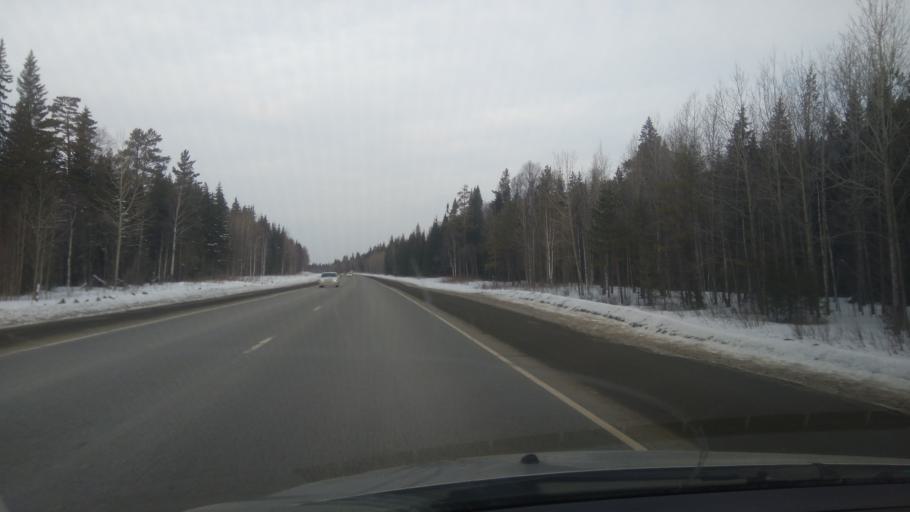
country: RU
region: Sverdlovsk
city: Atig
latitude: 56.8133
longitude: 59.3591
